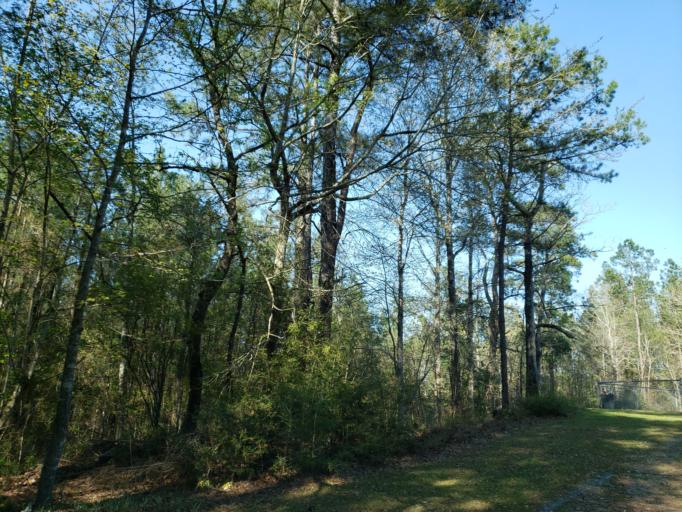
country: US
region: Mississippi
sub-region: Smith County
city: Taylorsville
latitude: 31.6898
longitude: -89.4183
